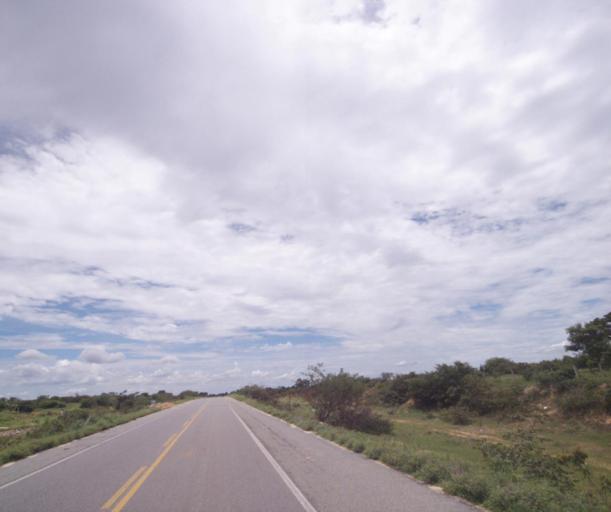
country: BR
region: Bahia
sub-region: Carinhanha
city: Carinhanha
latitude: -14.2999
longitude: -43.7854
